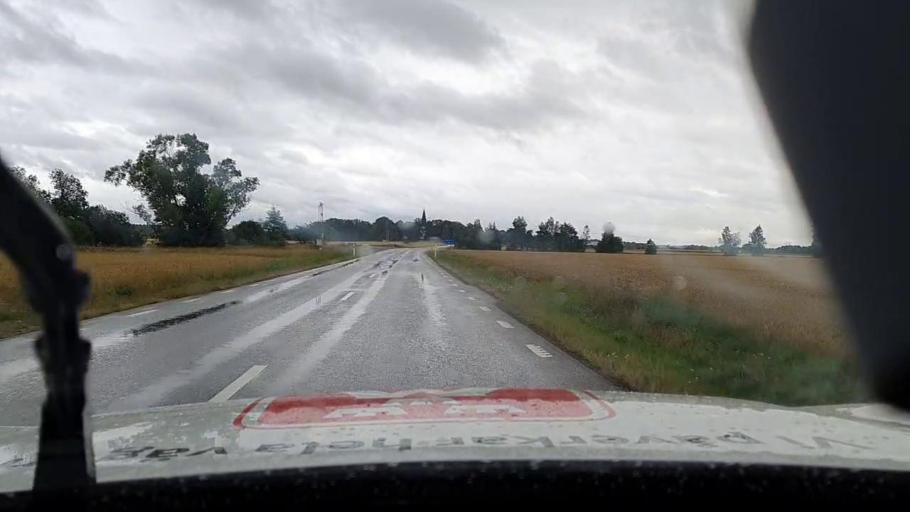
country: SE
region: Vaestra Goetaland
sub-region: Toreboda Kommun
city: Toereboda
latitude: 58.6140
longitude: 14.0107
